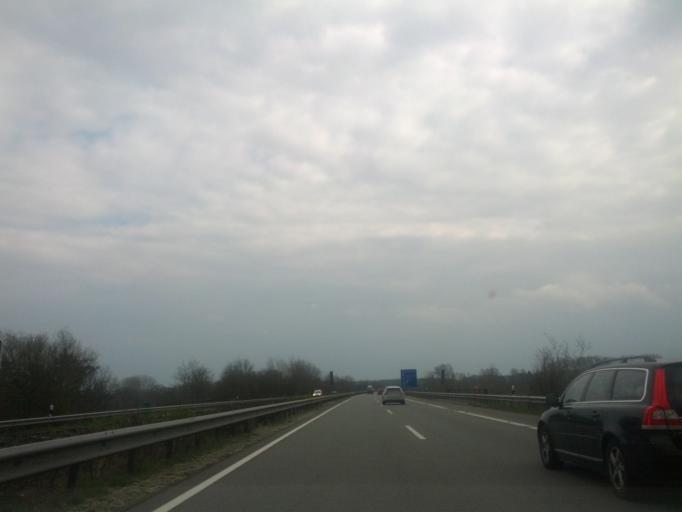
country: DE
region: Lower Saxony
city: Westerstede
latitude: 53.2834
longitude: 7.8910
